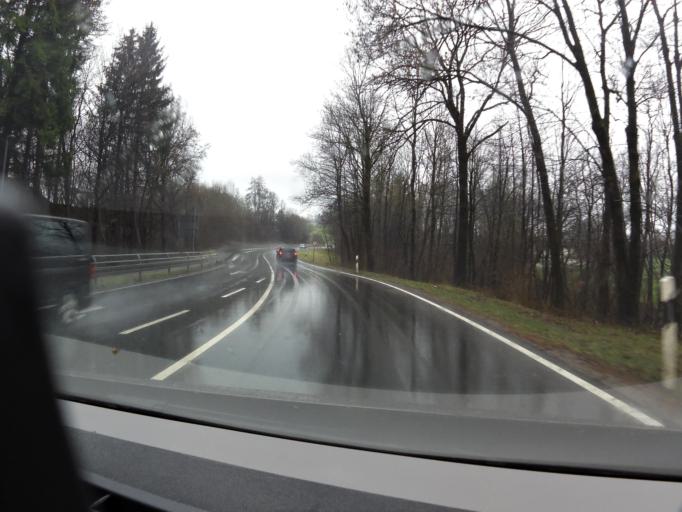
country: DE
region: Bavaria
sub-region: Upper Bavaria
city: Gaissach
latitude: 47.7591
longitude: 11.5775
